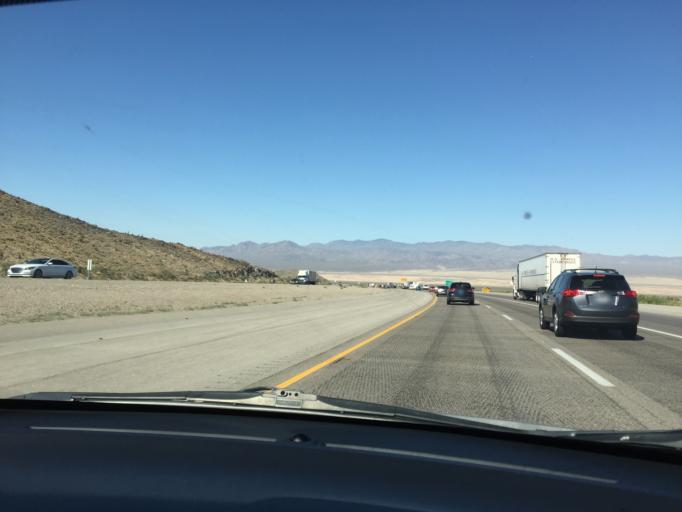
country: US
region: Nevada
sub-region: Clark County
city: Sandy Valley
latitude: 35.4617
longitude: -115.4666
